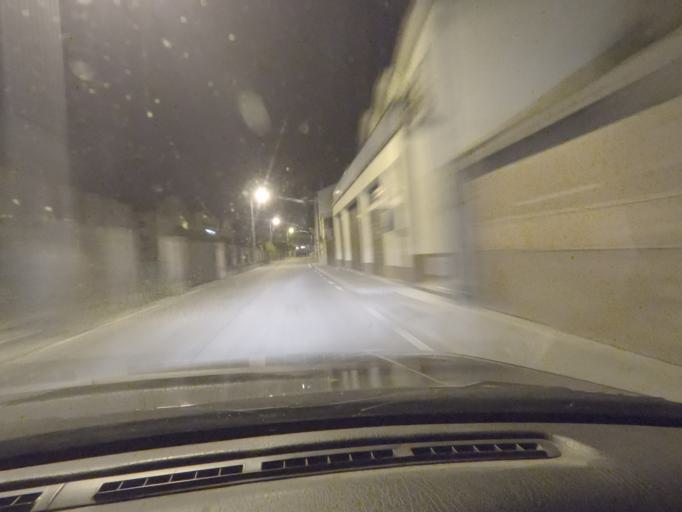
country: PT
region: Vila Real
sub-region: Peso da Regua
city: Godim
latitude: 41.1704
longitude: -7.7962
